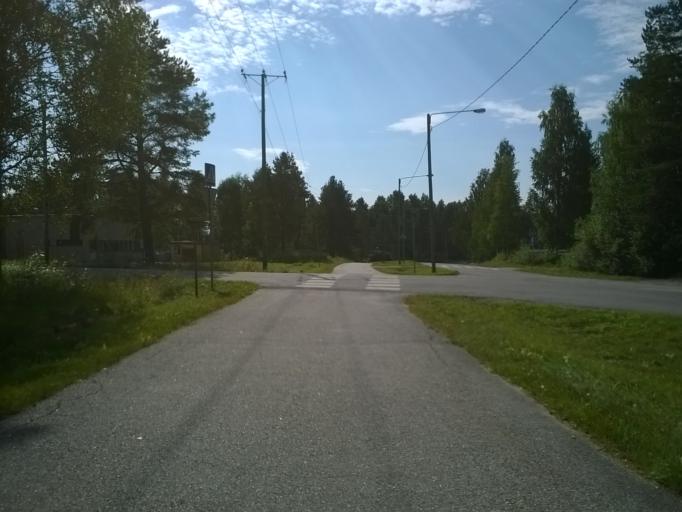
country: FI
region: Kainuu
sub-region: Kehys-Kainuu
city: Kuhmo
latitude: 64.1295
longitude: 29.4725
